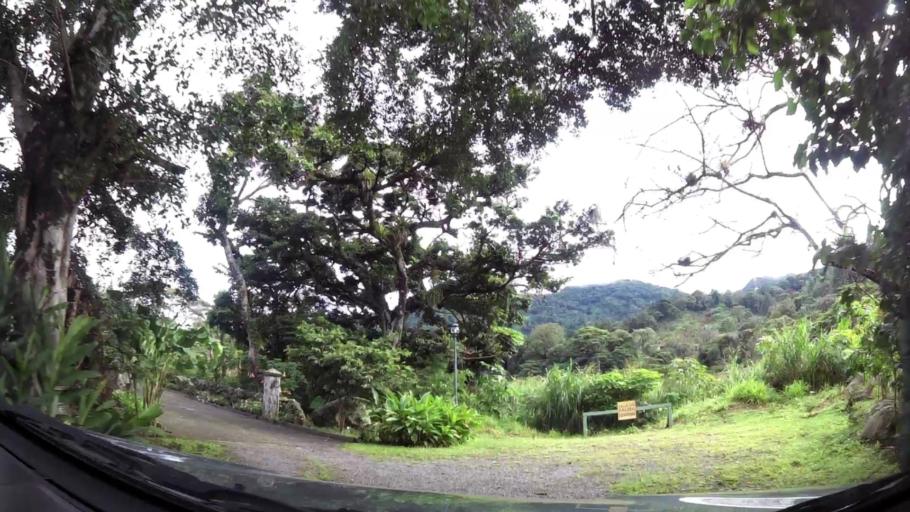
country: PA
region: Chiriqui
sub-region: Distrito Boquete
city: Boquete
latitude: 8.7843
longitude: -82.4306
